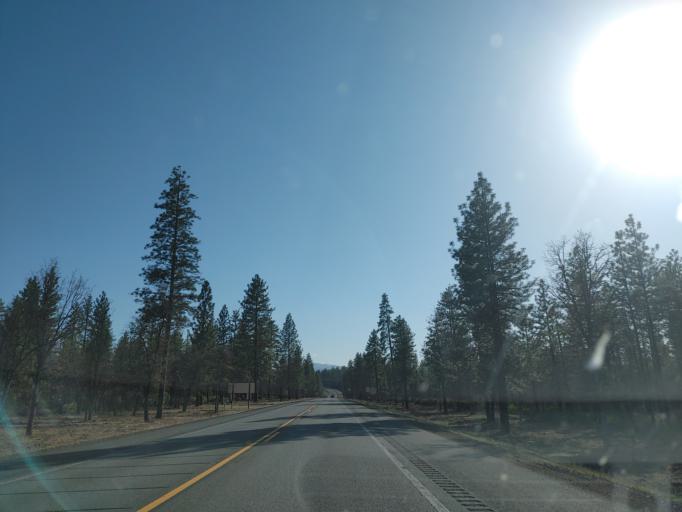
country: US
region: California
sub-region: Shasta County
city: Burney
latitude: 40.9367
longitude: -121.6084
